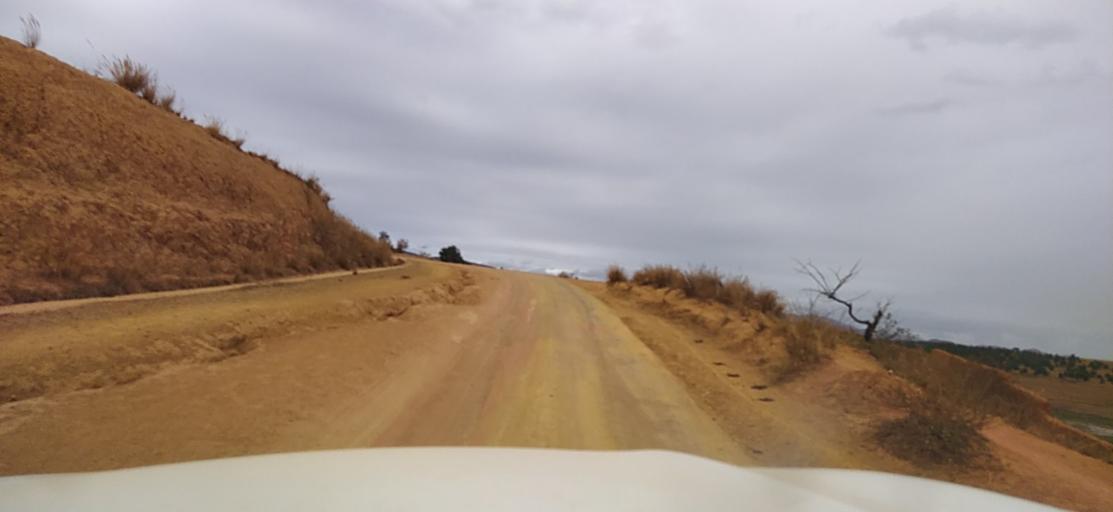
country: MG
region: Alaotra Mangoro
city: Ambatondrazaka
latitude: -17.9126
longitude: 48.2637
